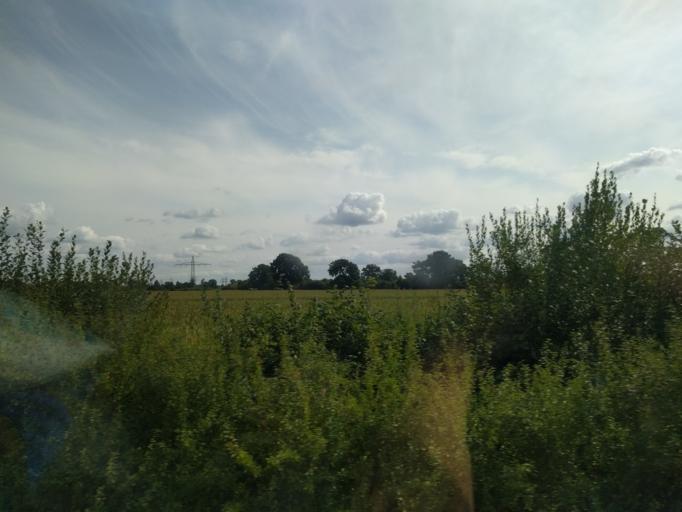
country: DE
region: Schleswig-Holstein
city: Hamberge
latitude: 53.8327
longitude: 10.5895
